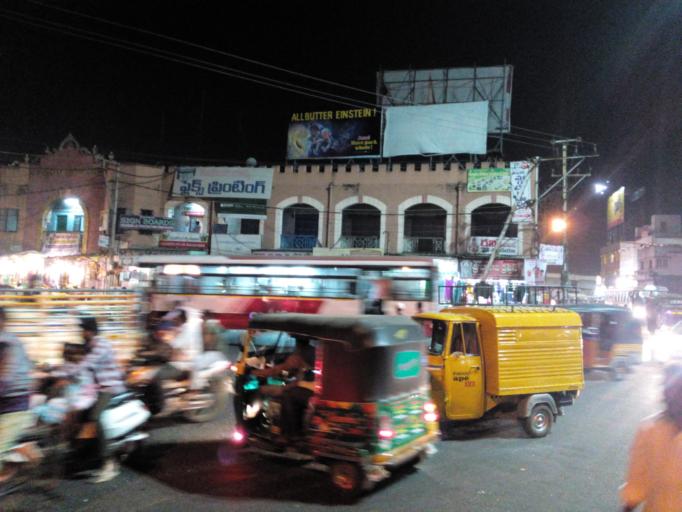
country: IN
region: Andhra Pradesh
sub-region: Krishna
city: Vijayawada
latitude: 16.5175
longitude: 80.6197
